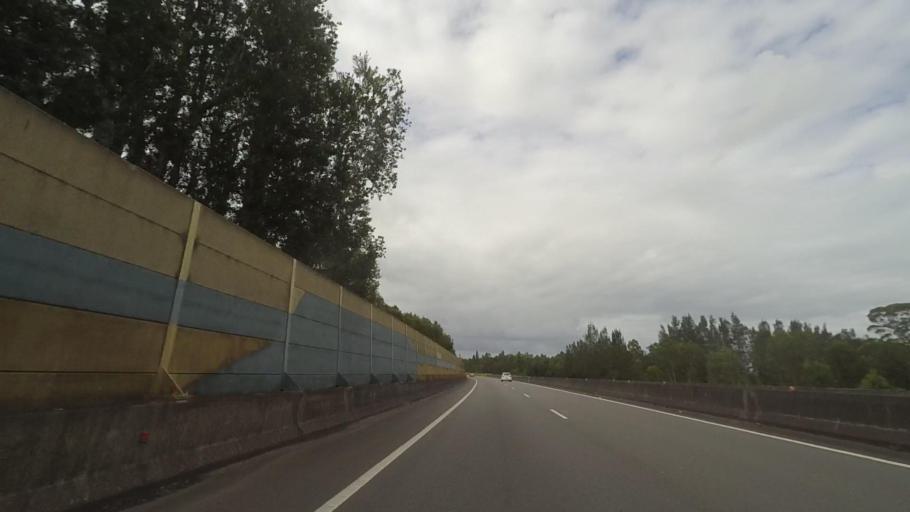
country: AU
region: New South Wales
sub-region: Port Stephens Shire
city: Raymond Terrace
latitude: -32.7699
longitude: 151.7614
